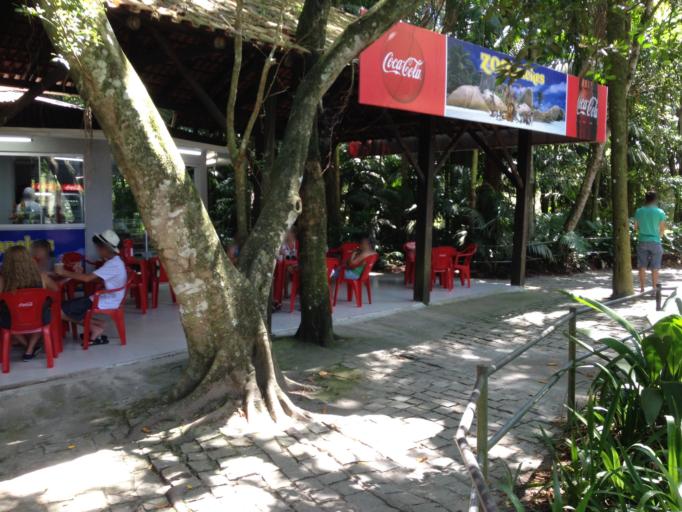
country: BR
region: Santa Catarina
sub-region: Balneario Camboriu
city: Balneario Camboriu
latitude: -27.0141
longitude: -48.6157
